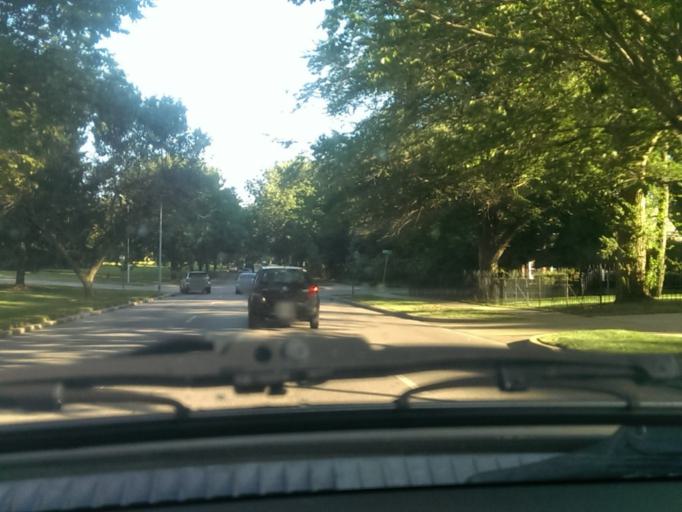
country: US
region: Kansas
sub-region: Johnson County
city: Mission Hills
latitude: 39.0251
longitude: -94.6028
